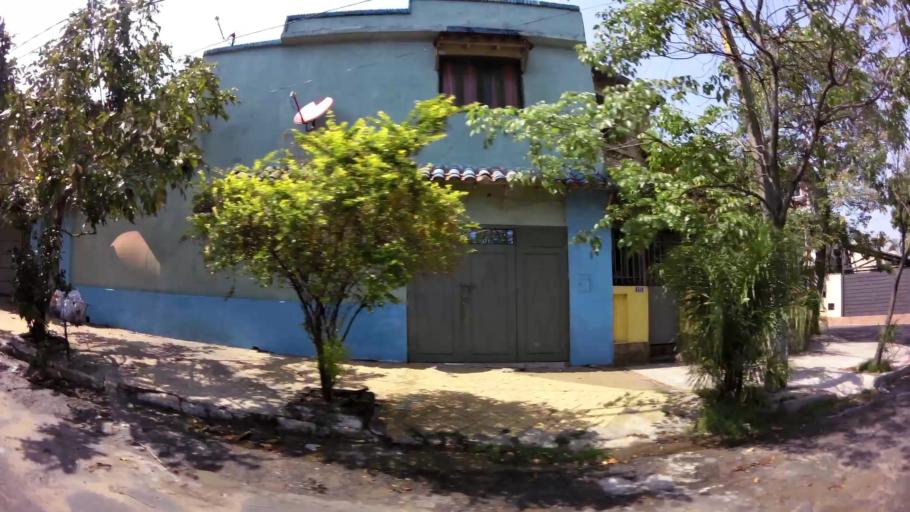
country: PY
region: Asuncion
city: Asuncion
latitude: -25.2893
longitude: -57.6506
